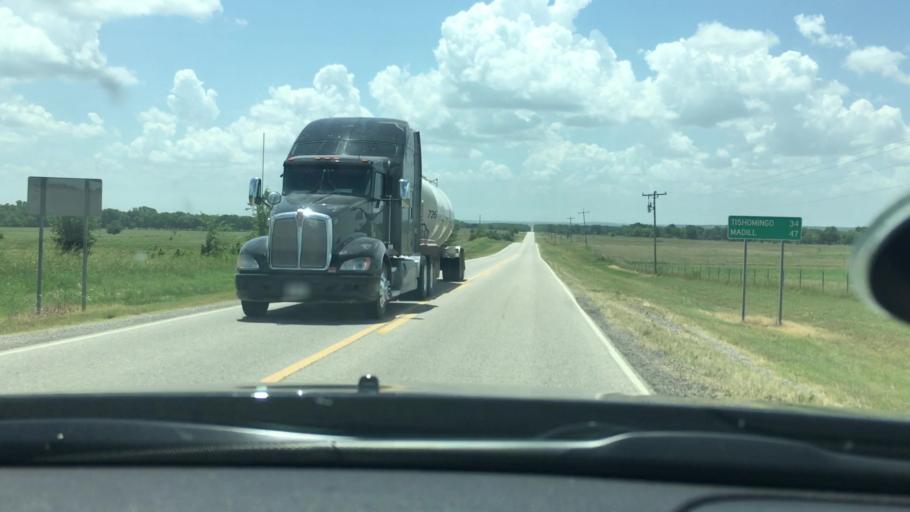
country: US
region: Oklahoma
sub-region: Pontotoc County
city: Ada
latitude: 34.7232
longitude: -96.6349
